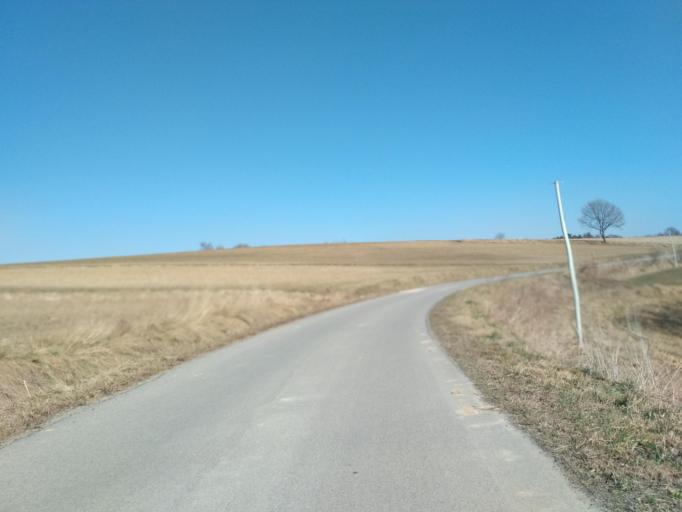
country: PL
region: Subcarpathian Voivodeship
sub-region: Powiat ropczycko-sedziszowski
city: Niedzwiada
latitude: 49.9560
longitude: 21.5477
